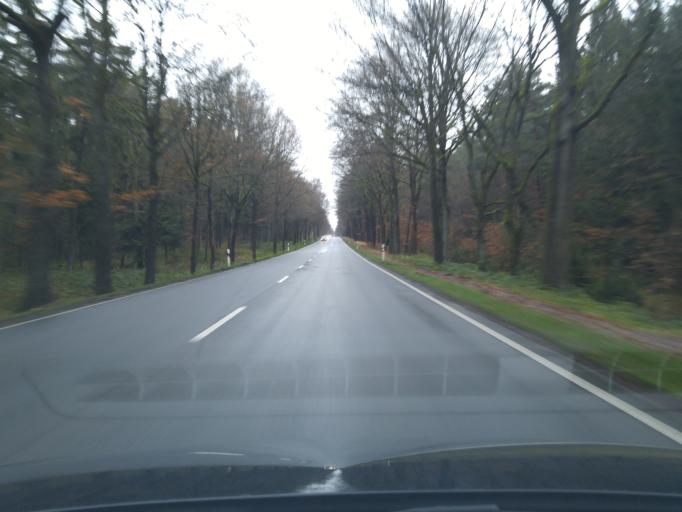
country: DE
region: Lower Saxony
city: Sprakensehl
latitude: 52.7931
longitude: 10.4897
